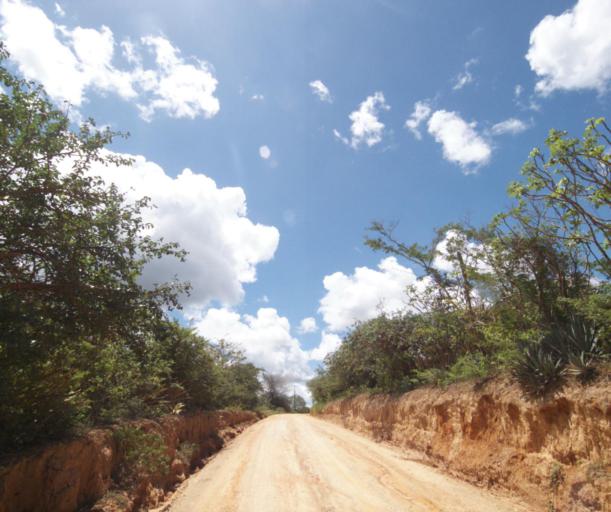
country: BR
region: Bahia
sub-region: Pocoes
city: Pocoes
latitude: -14.3884
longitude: -40.5500
